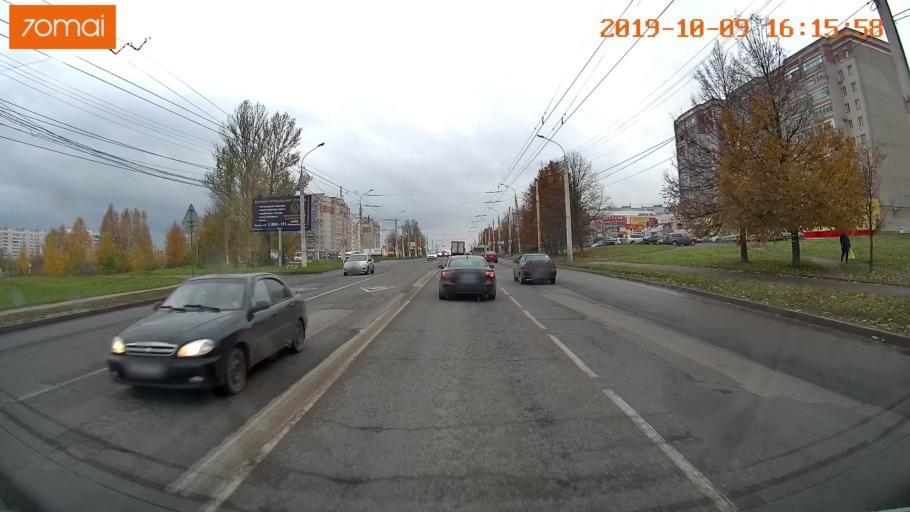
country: RU
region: Kostroma
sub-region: Kostromskoy Rayon
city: Kostroma
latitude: 57.7376
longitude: 40.9127
